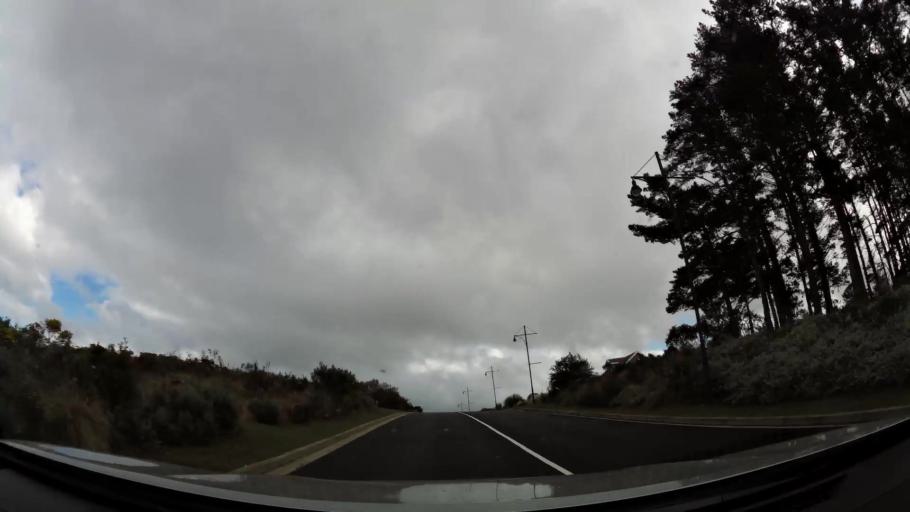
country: ZA
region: Western Cape
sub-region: Eden District Municipality
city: Knysna
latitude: -34.0659
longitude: 23.1019
